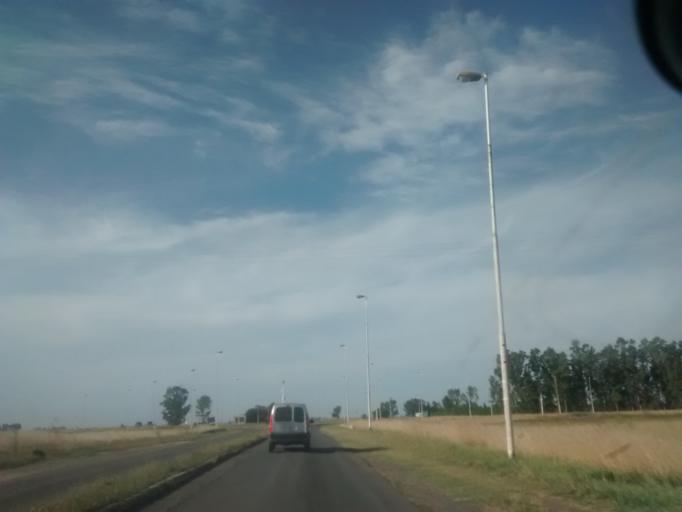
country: AR
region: Buenos Aires
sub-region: Partido de Ayacucho
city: Ayacucho
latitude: -37.1291
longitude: -58.5516
